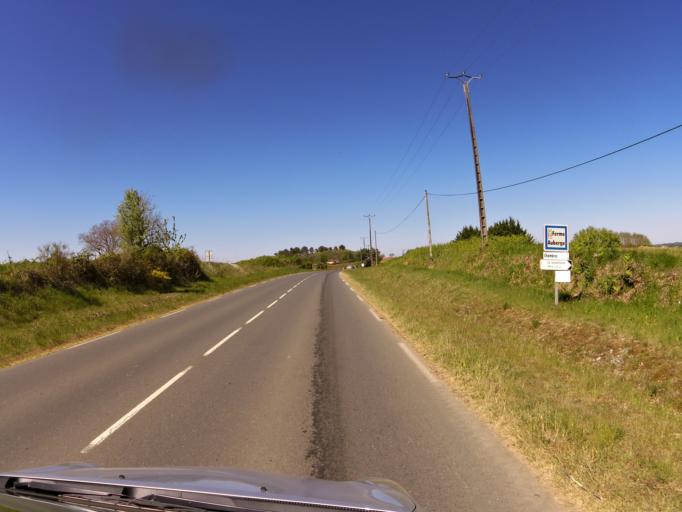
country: FR
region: Aquitaine
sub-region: Departement de la Dordogne
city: Sarlat-la-Caneda
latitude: 44.9735
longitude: 1.2373
